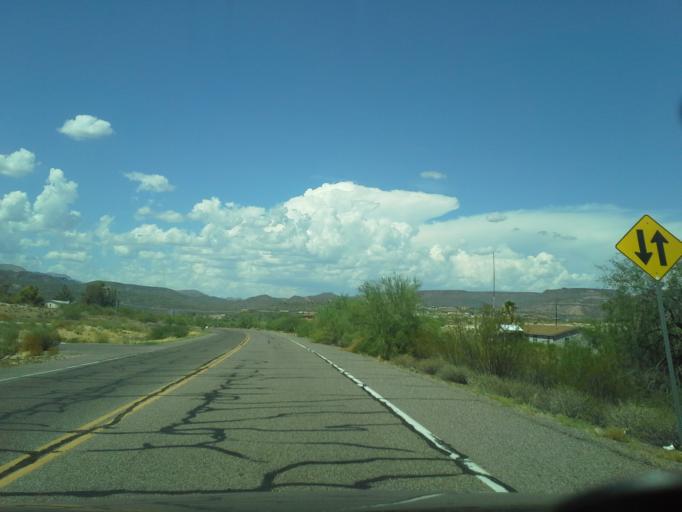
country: US
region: Arizona
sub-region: Yavapai County
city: Black Canyon City
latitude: 34.0593
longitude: -112.1464
